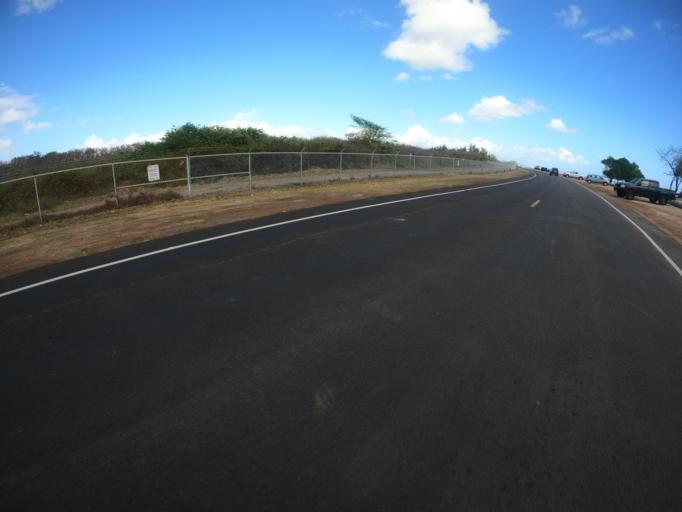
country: US
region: Hawaii
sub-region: Honolulu County
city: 'Ewa Villages
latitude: 21.3005
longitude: -158.0640
